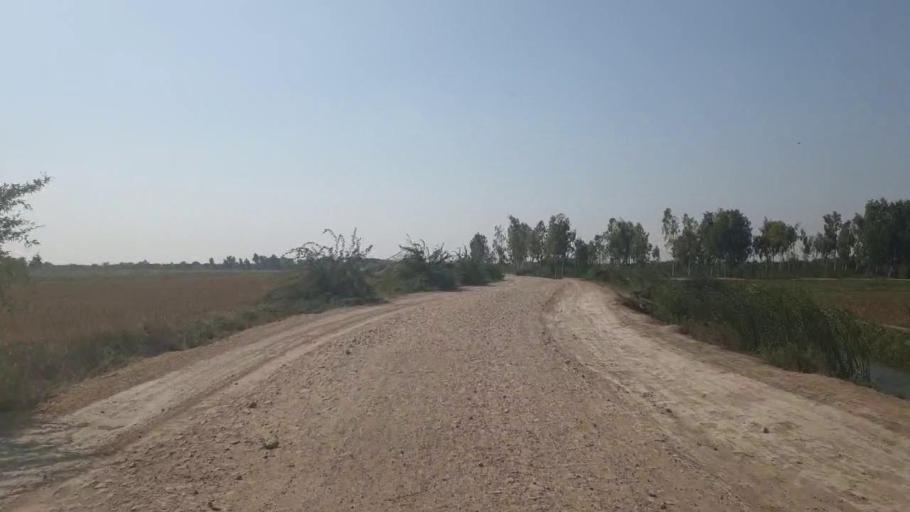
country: PK
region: Sindh
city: Badin
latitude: 24.5952
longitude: 68.8528
